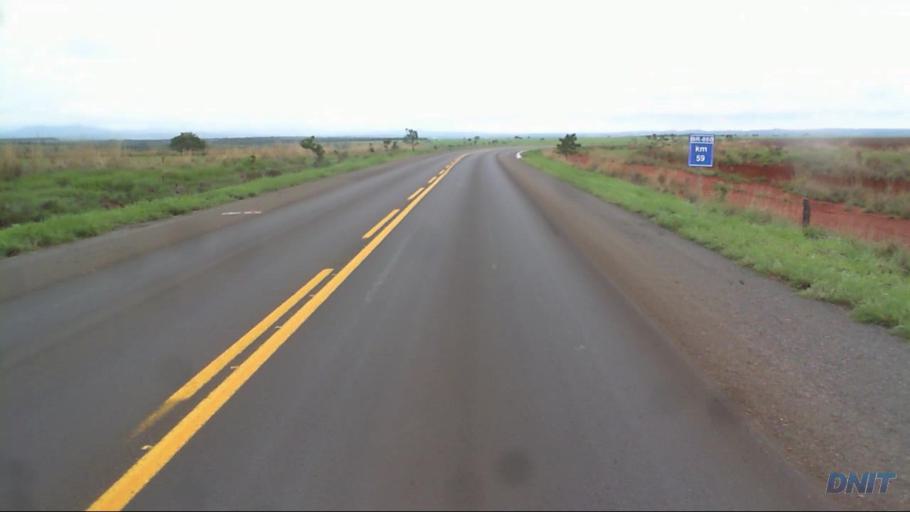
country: BR
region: Goias
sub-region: Padre Bernardo
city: Padre Bernardo
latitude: -15.1733
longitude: -48.3928
